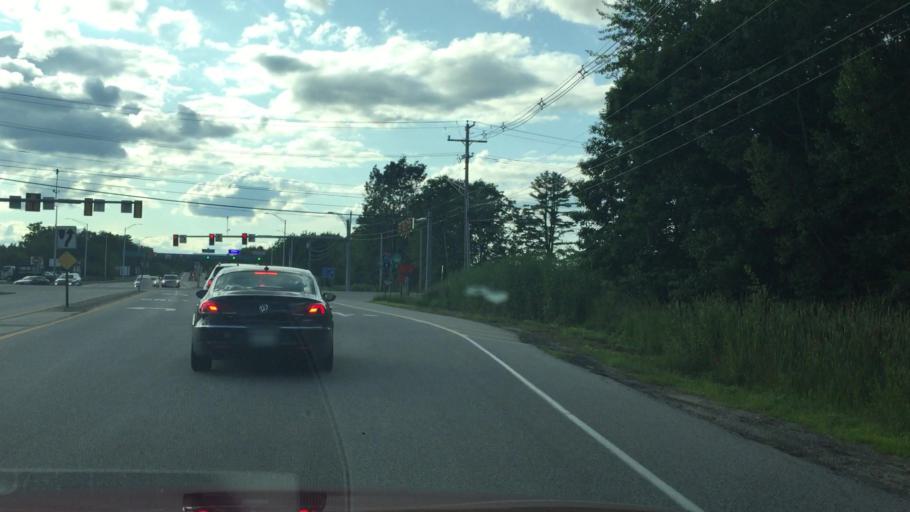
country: US
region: Maine
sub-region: Cumberland County
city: West Scarborough
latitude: 43.6027
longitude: -70.3654
